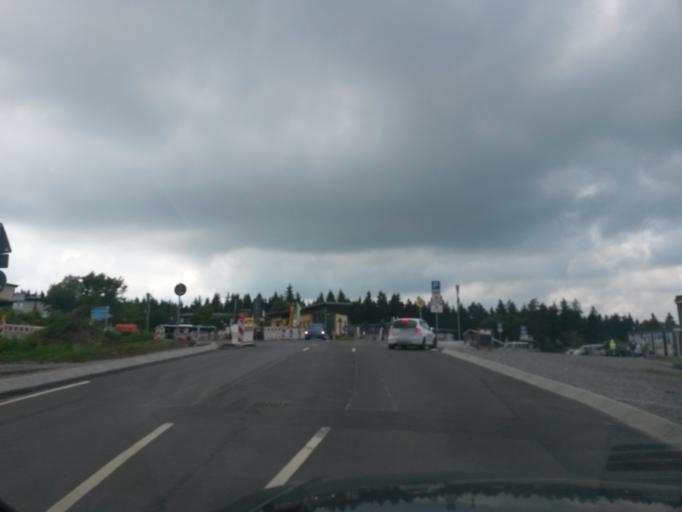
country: DE
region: Hesse
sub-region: Regierungsbezirk Kassel
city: Gersfeld
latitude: 50.4977
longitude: 9.9480
